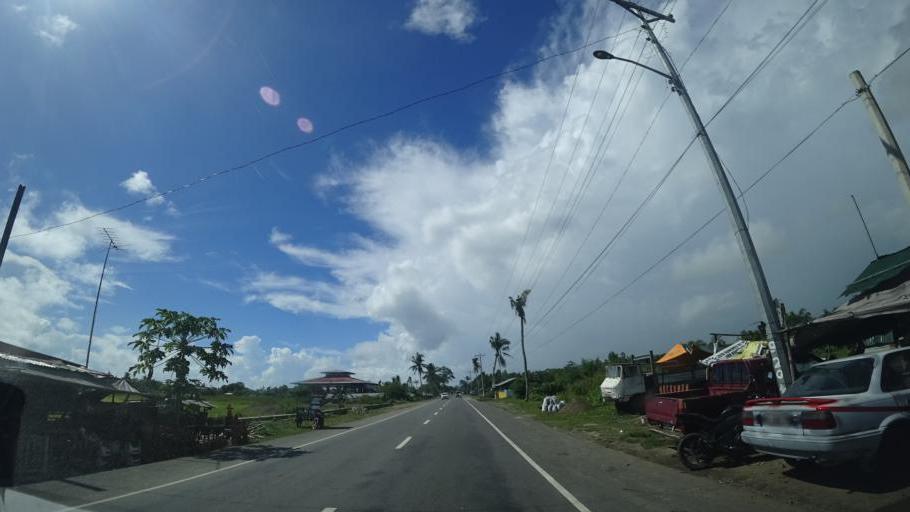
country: PH
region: Eastern Visayas
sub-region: Province of Leyte
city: Tanauan
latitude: 11.1183
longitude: 125.0170
